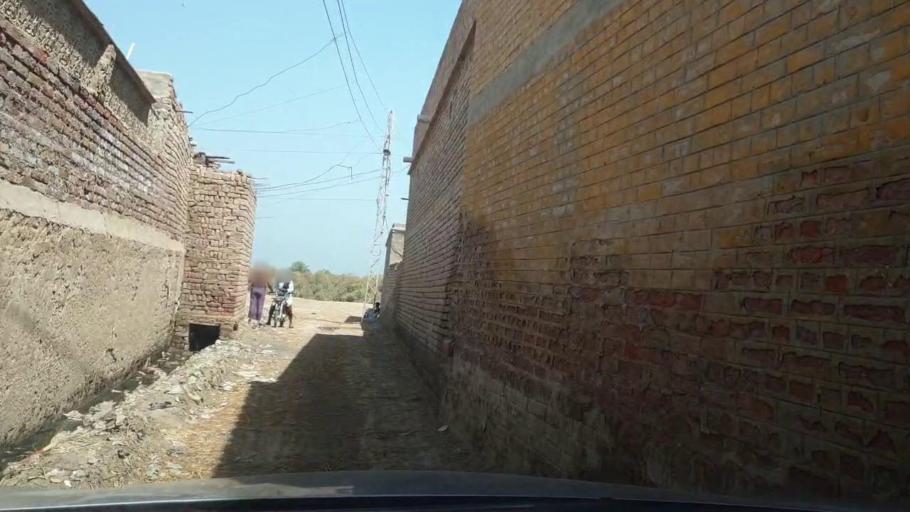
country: PK
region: Sindh
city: Kambar
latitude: 27.5906
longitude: 67.9097
